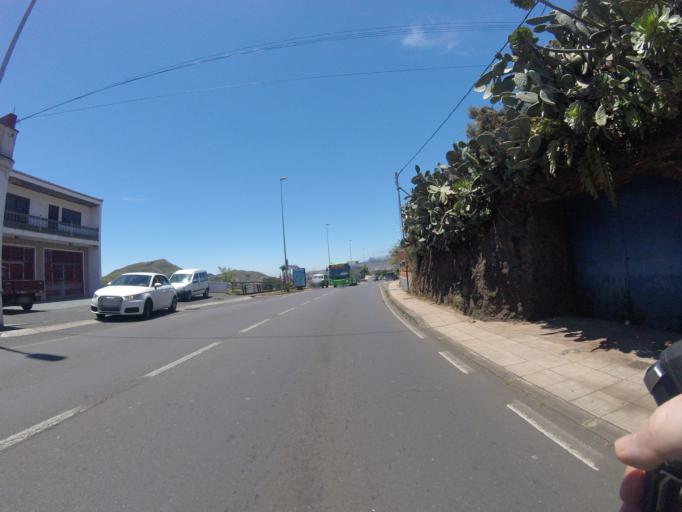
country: ES
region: Canary Islands
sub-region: Provincia de Santa Cruz de Tenerife
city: Tegueste
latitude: 28.5121
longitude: -16.3062
